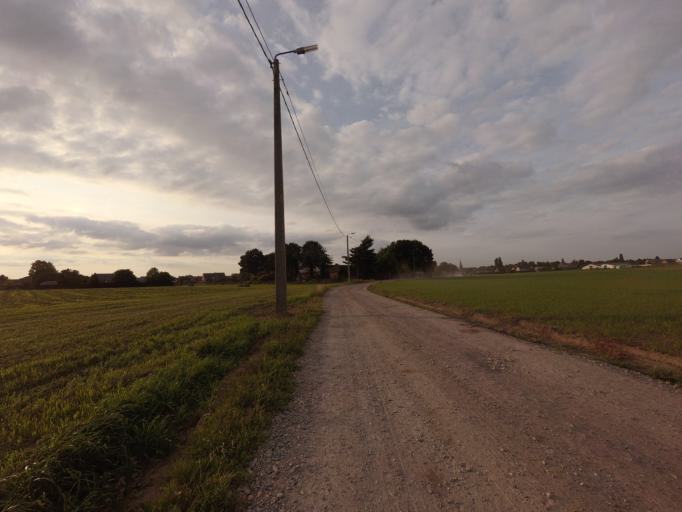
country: BE
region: Flanders
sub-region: Provincie Vlaams-Brabant
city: Kampenhout
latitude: 50.9329
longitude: 4.5481
